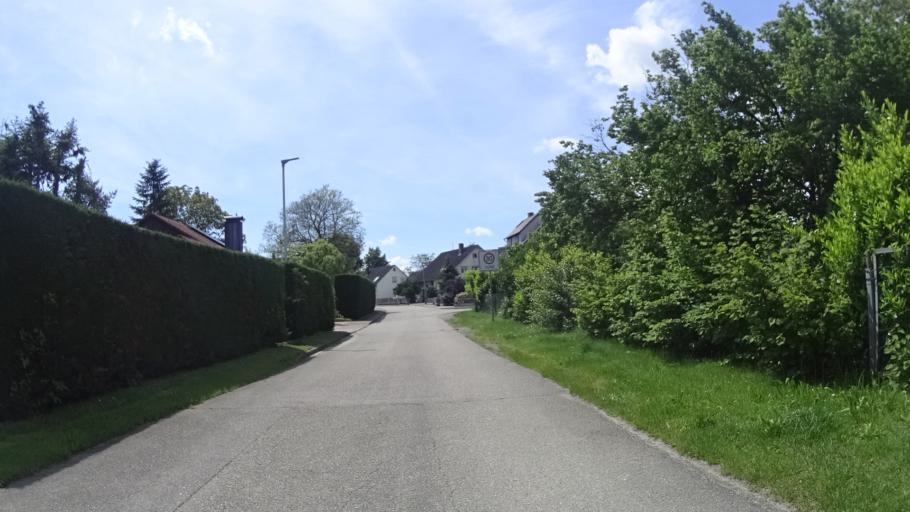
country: DE
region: Baden-Wuerttemberg
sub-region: Freiburg Region
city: Schwanau
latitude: 48.3545
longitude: 7.7537
